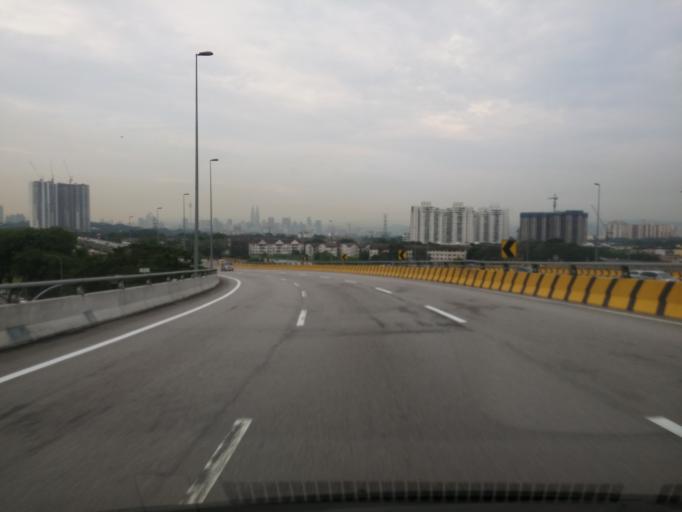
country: MY
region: Kuala Lumpur
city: Kuala Lumpur
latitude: 3.0899
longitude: 101.6962
